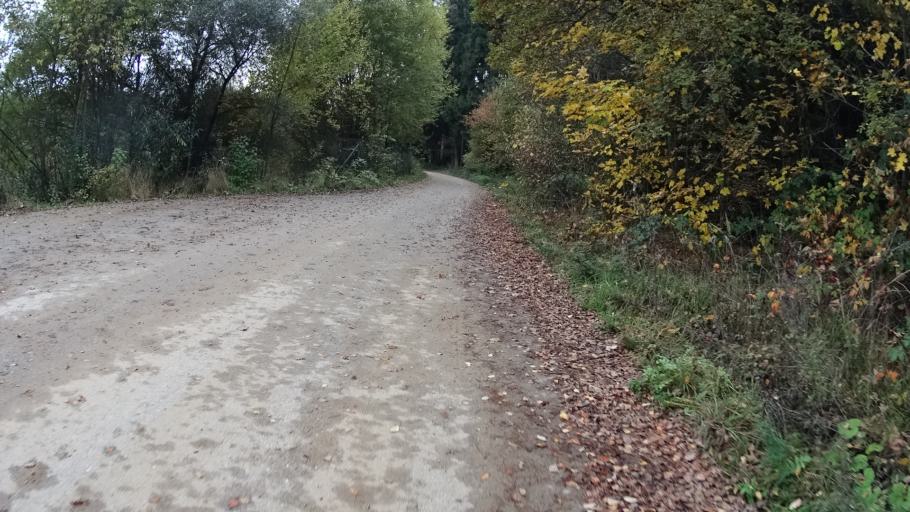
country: DE
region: Bavaria
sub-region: Upper Bavaria
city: Hitzhofen
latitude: 48.8507
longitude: 11.2993
